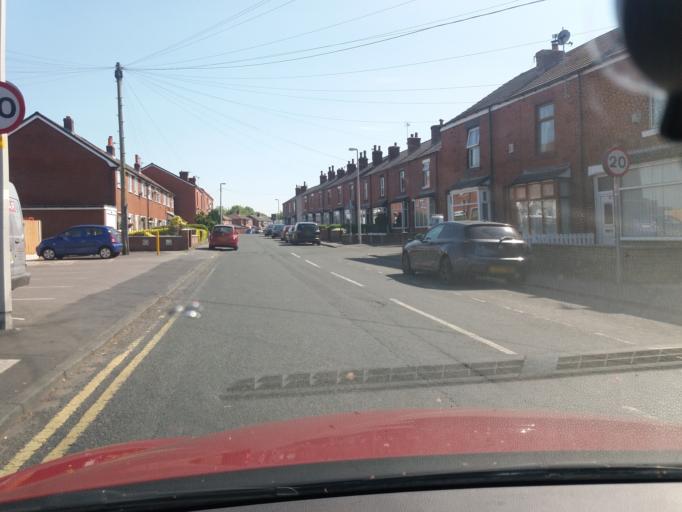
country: GB
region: England
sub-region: Lancashire
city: Coppull
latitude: 53.6272
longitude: -2.6559
